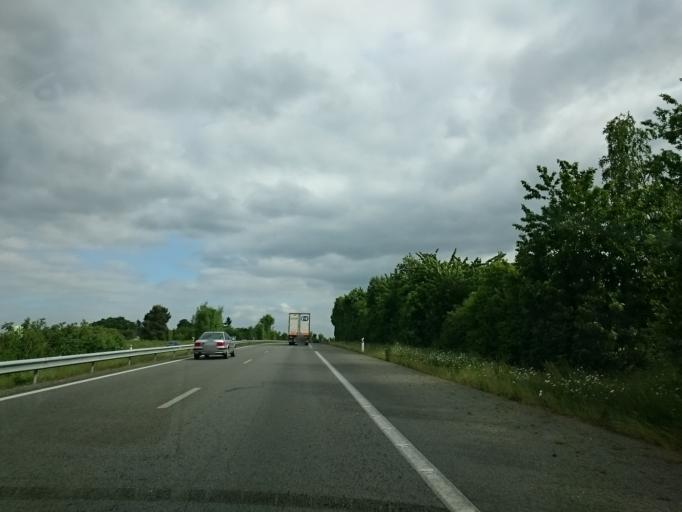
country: FR
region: Brittany
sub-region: Departement d'Ille-et-Vilaine
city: Crevin
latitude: 47.9538
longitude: -1.6808
